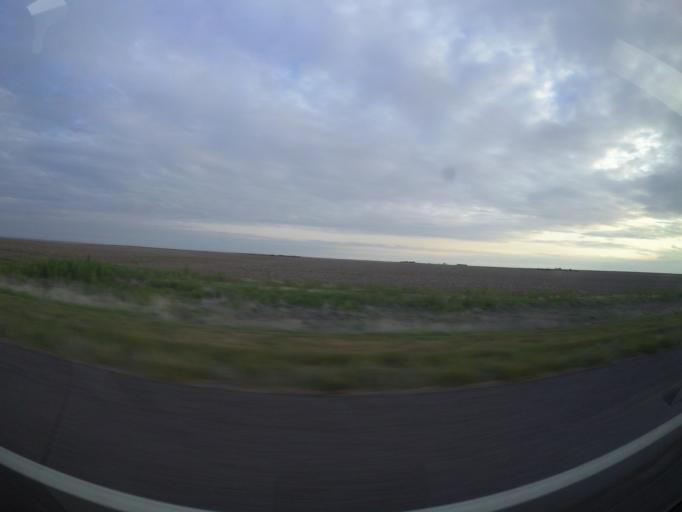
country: US
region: Kansas
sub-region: Cheyenne County
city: Saint Francis
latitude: 39.7461
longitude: -102.1171
